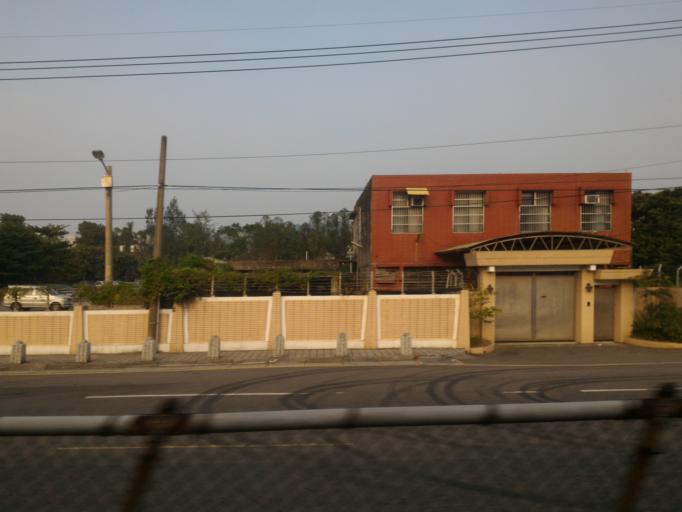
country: TW
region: Taiwan
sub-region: Taoyuan
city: Taoyuan
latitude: 24.9777
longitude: 121.3314
